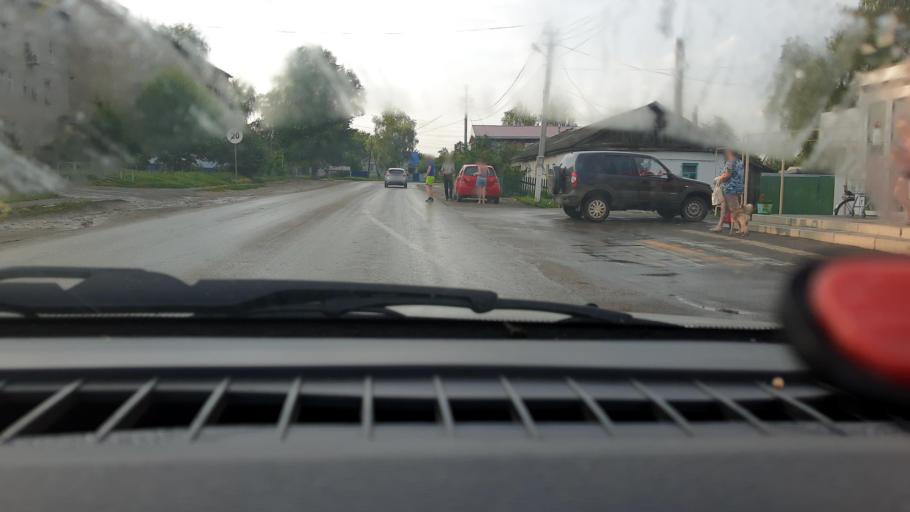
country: RU
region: Nizjnij Novgorod
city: Lukoyanov
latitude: 55.0365
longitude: 44.4944
